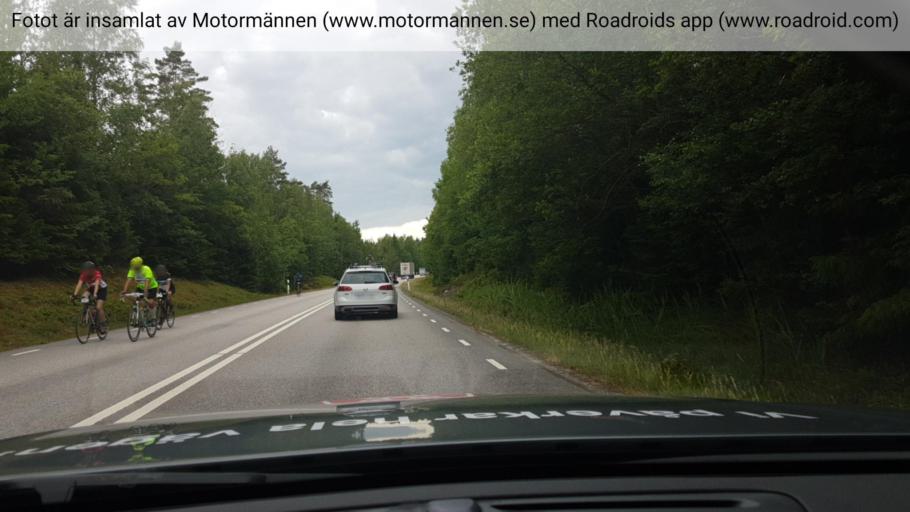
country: SE
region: Vaestra Goetaland
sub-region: Karlsborgs Kommun
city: Karlsborg
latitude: 58.6872
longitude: 14.6718
